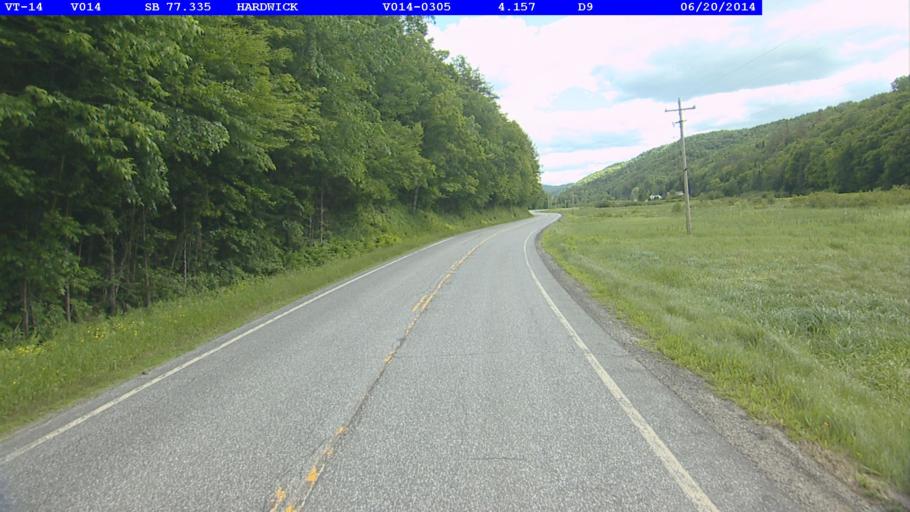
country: US
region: Vermont
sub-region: Caledonia County
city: Hardwick
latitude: 44.5534
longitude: -72.3694
